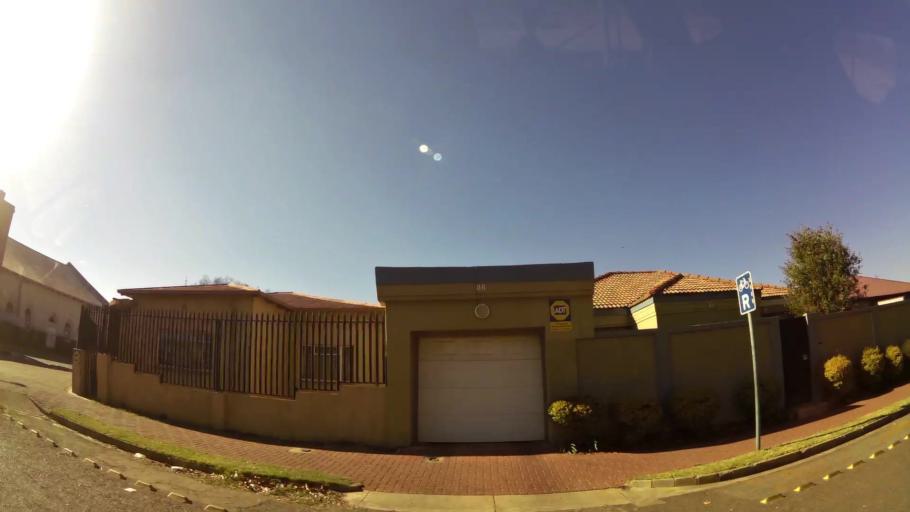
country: ZA
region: Gauteng
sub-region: City of Johannesburg Metropolitan Municipality
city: Johannesburg
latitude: -26.1942
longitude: 27.9959
